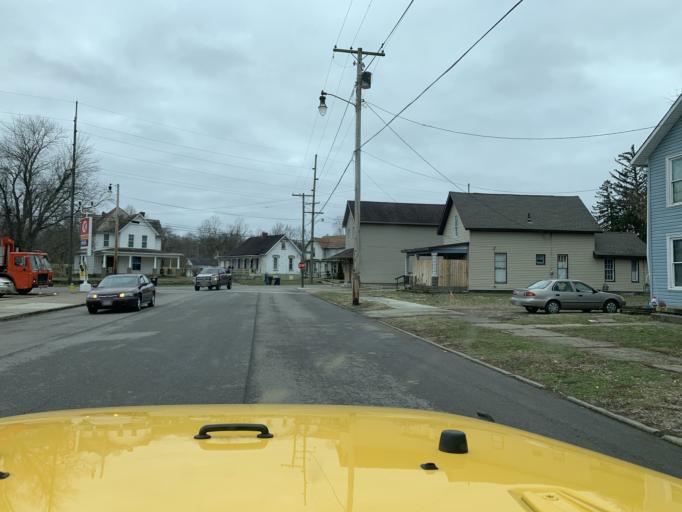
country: US
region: Ohio
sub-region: Licking County
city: Newark
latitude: 40.0496
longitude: -82.4026
